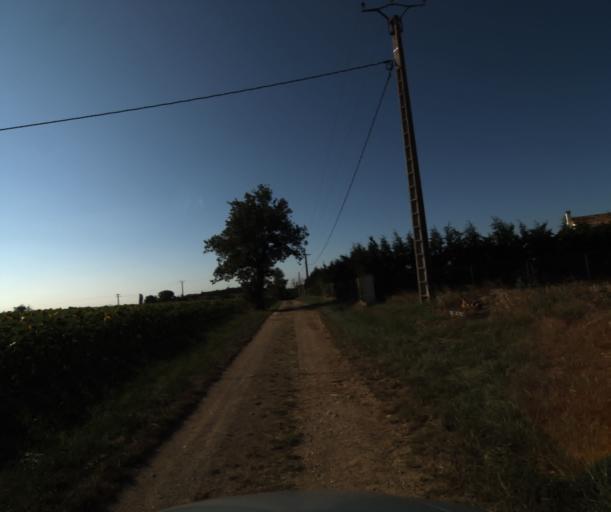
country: FR
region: Midi-Pyrenees
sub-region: Departement de la Haute-Garonne
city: Labarthe-sur-Leze
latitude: 43.4453
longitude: 1.3744
